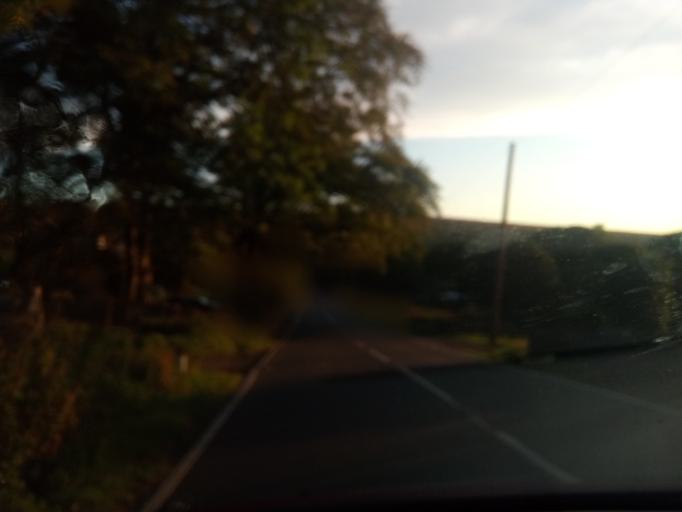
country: GB
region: England
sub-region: Northumberland
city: Bardon Mill
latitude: 54.7875
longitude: -2.3360
